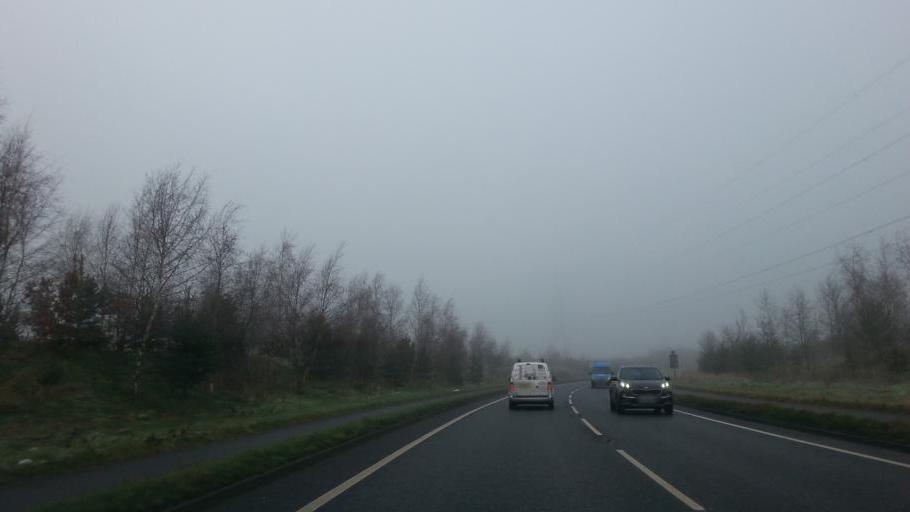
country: GB
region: England
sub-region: Cheshire East
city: Alderley Edge
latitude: 53.2913
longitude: -2.2555
